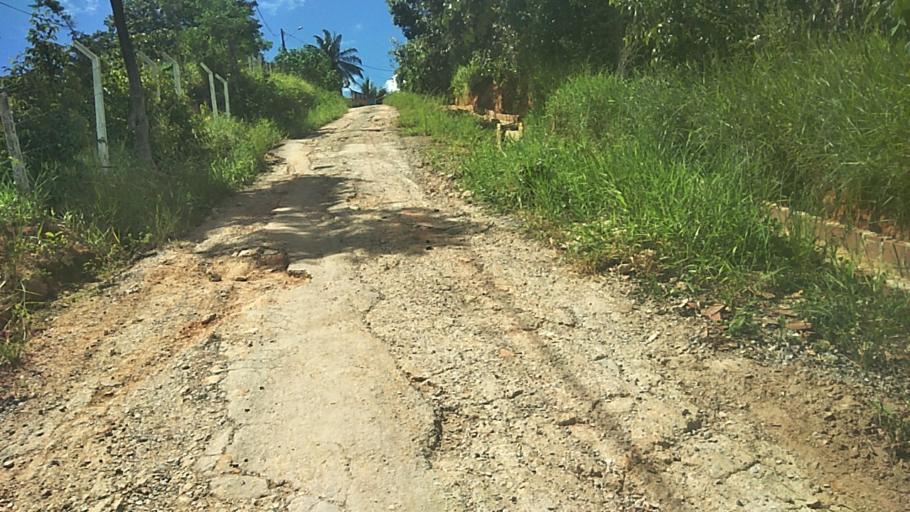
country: BR
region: Pernambuco
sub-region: Jaboatao Dos Guararapes
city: Jaboatao dos Guararapes
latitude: -8.0709
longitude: -35.0059
